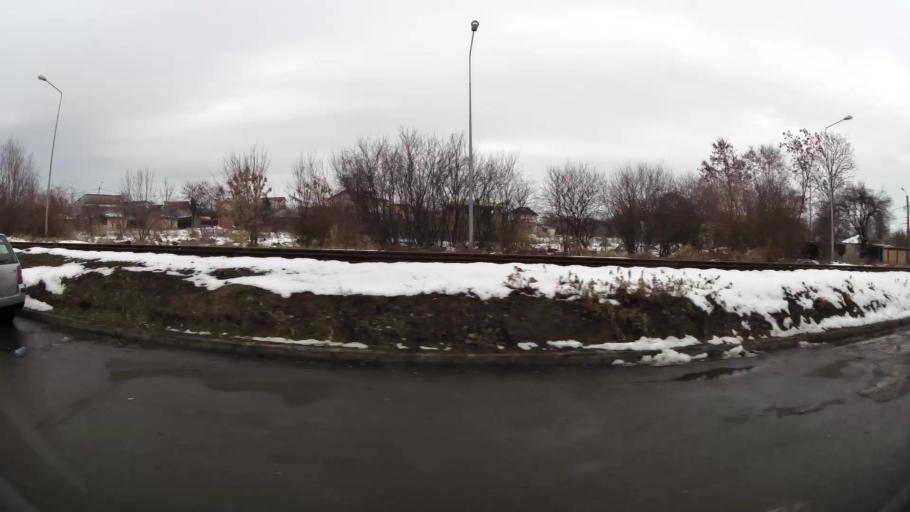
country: RO
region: Ilfov
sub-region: Comuna Pantelimon
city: Pantelimon
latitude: 44.4282
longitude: 26.2105
